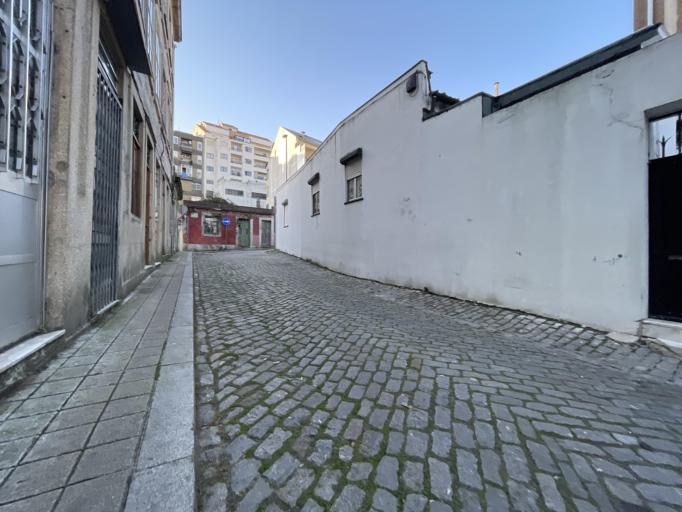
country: PT
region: Porto
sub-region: Porto
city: Porto
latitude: 41.1561
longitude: -8.5981
